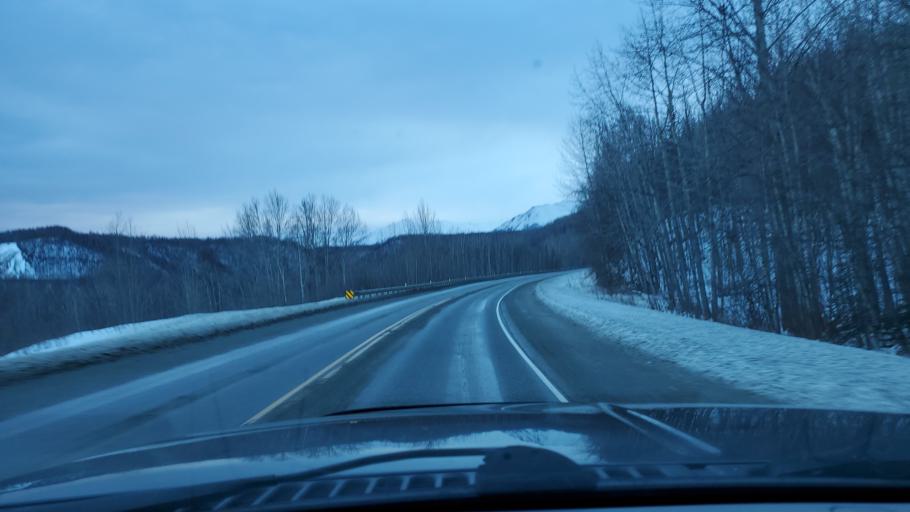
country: US
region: Alaska
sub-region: Matanuska-Susitna Borough
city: Lazy Mountain
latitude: 61.6787
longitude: -149.0285
